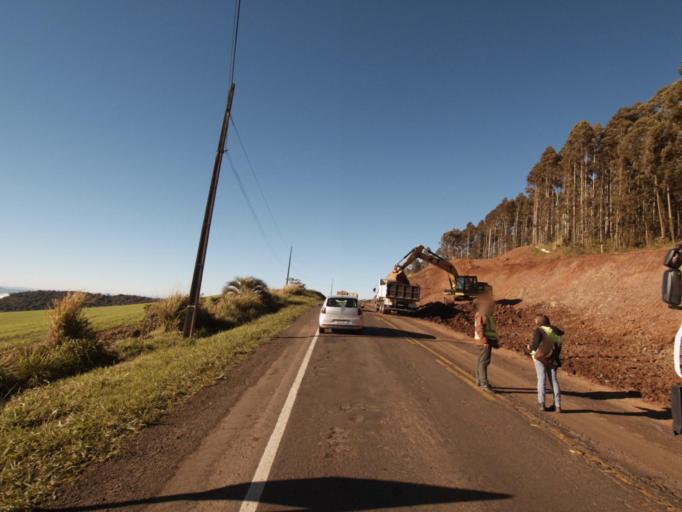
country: AR
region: Misiones
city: Bernardo de Irigoyen
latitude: -26.6214
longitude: -53.5171
